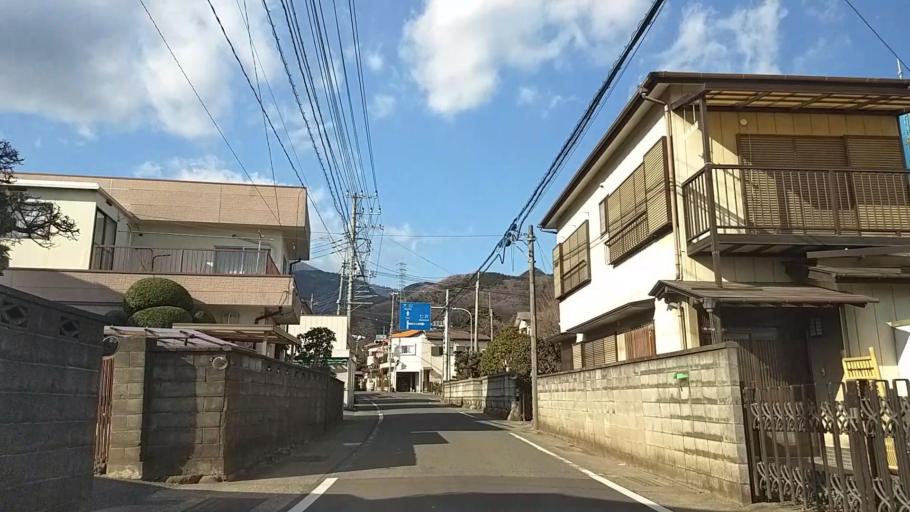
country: JP
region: Kanagawa
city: Isehara
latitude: 35.4133
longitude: 139.2849
